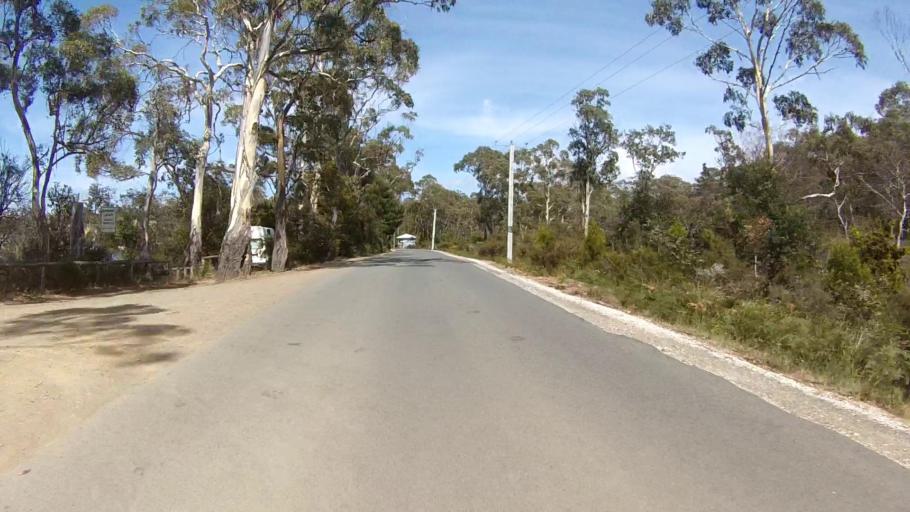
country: AU
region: Tasmania
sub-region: Huon Valley
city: Cygnet
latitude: -43.2428
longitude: 147.1215
